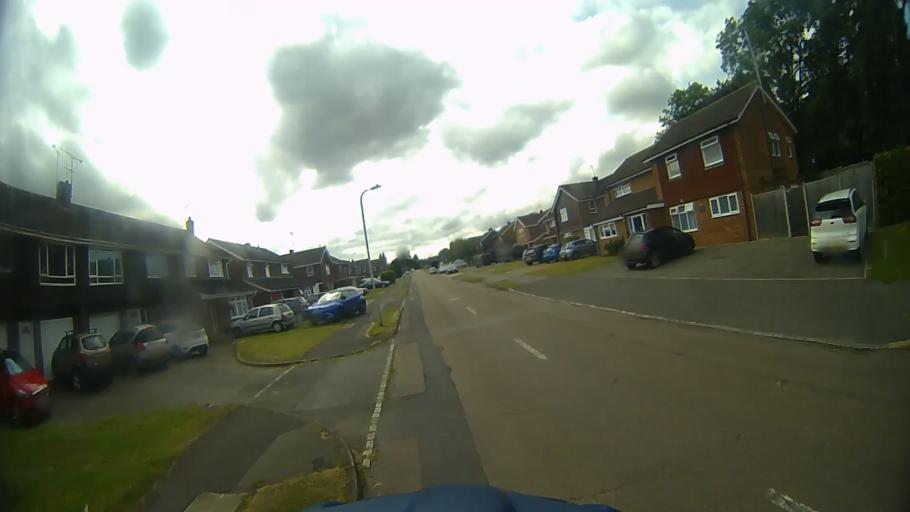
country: GB
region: England
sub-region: Wokingham
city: Woodley
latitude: 51.4500
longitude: -0.8946
